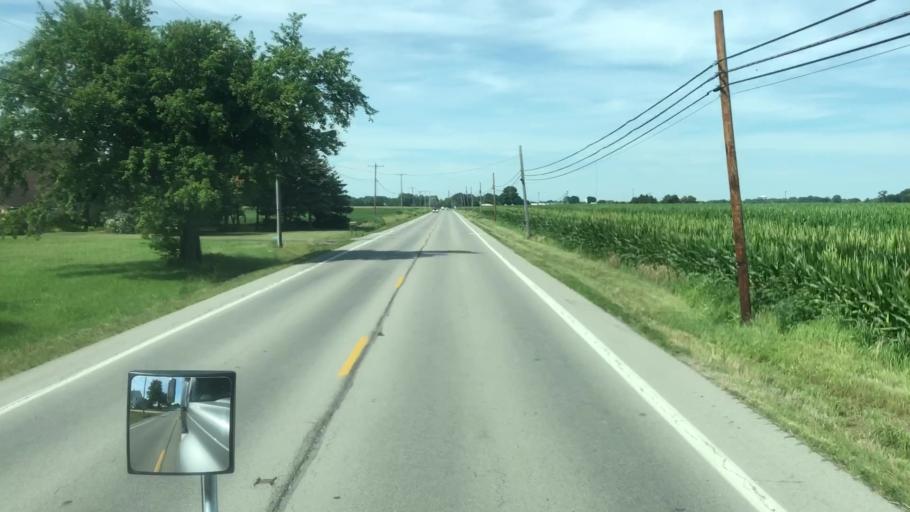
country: US
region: Ohio
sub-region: Sandusky County
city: Fremont
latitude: 41.3752
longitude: -83.0640
